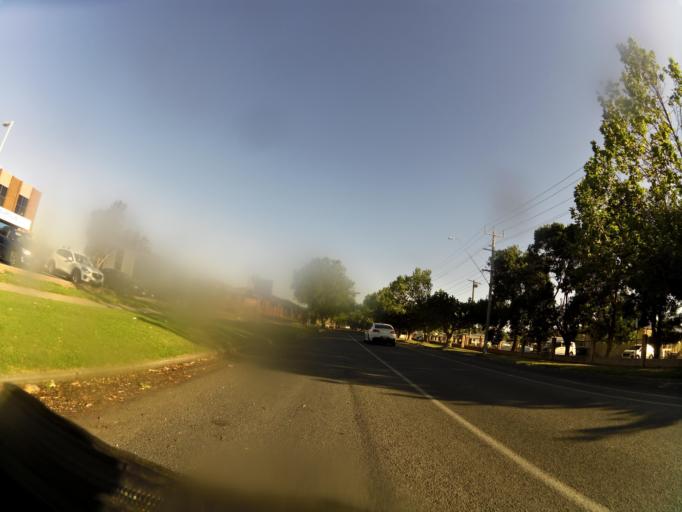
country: AU
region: Victoria
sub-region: Murrindindi
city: Kinglake West
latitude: -37.0219
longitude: 145.1312
